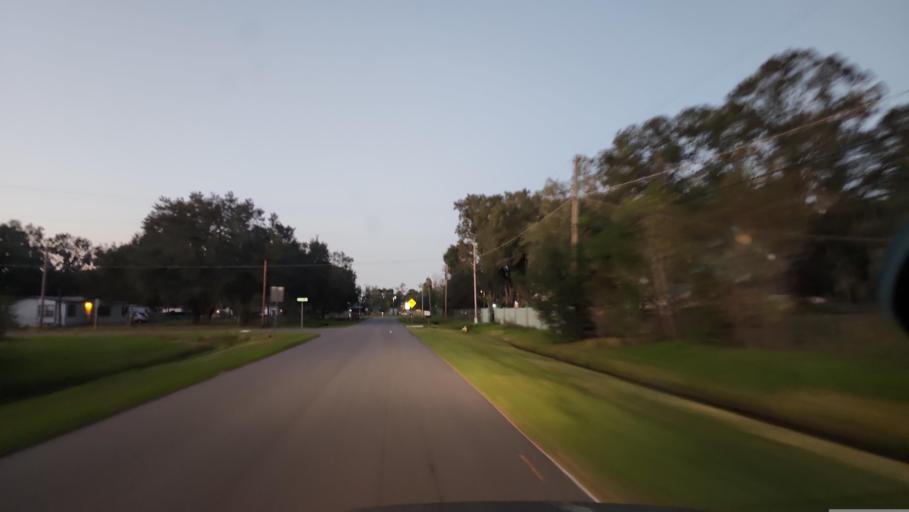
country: US
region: Florida
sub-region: Hillsborough County
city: Boyette
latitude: 27.8112
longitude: -82.2747
